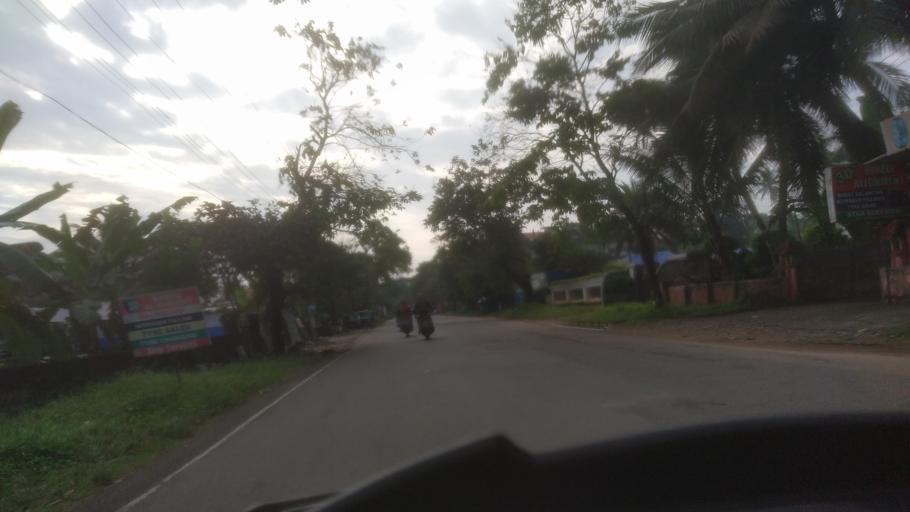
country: IN
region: Kerala
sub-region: Ernakulam
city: Kotamangalam
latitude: 10.0650
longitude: 76.6318
